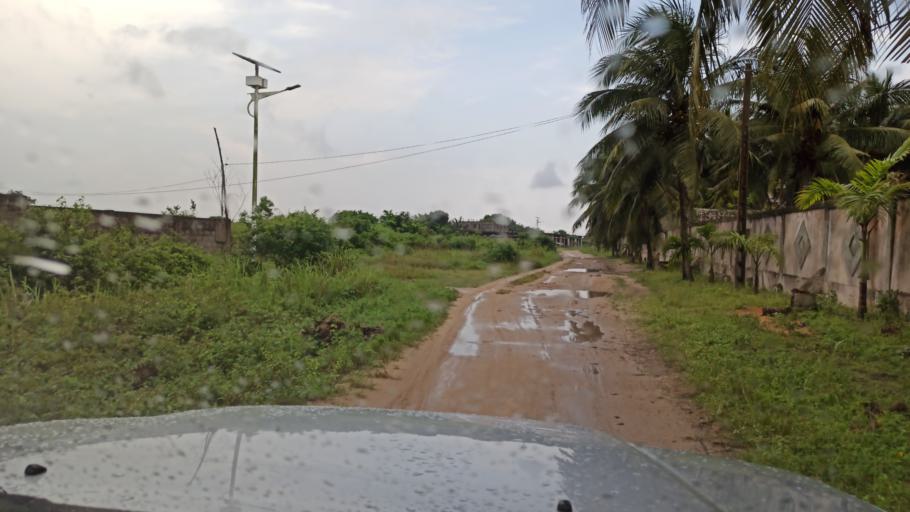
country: BJ
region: Queme
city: Porto-Novo
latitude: 6.4510
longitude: 2.6637
